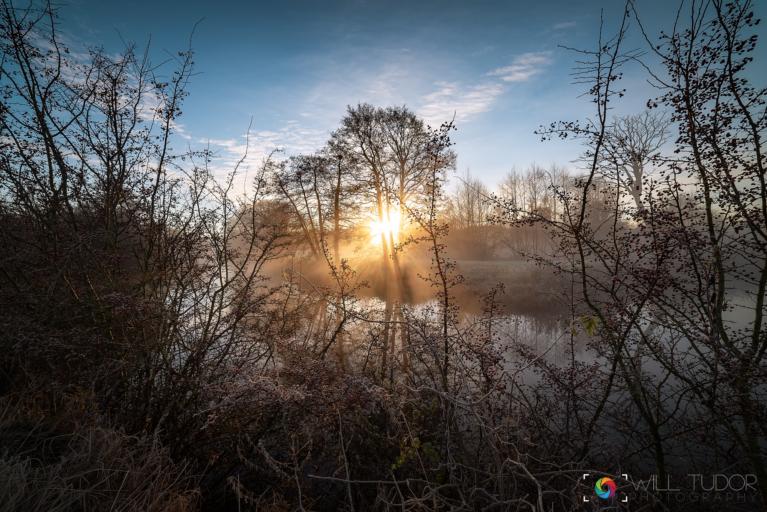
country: GB
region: England
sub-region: Warwickshire
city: Alcester
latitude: 52.2095
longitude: -1.8760
